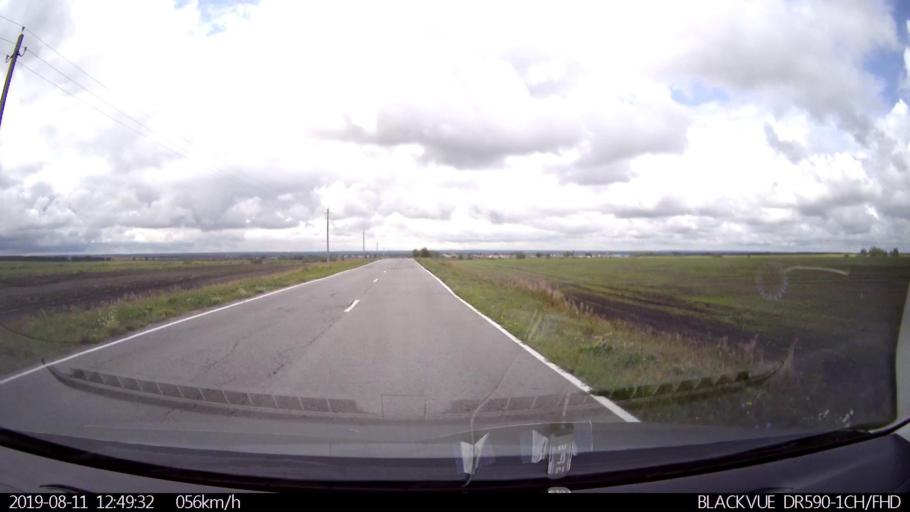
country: RU
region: Ulyanovsk
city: Ignatovka
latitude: 53.8747
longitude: 47.6852
